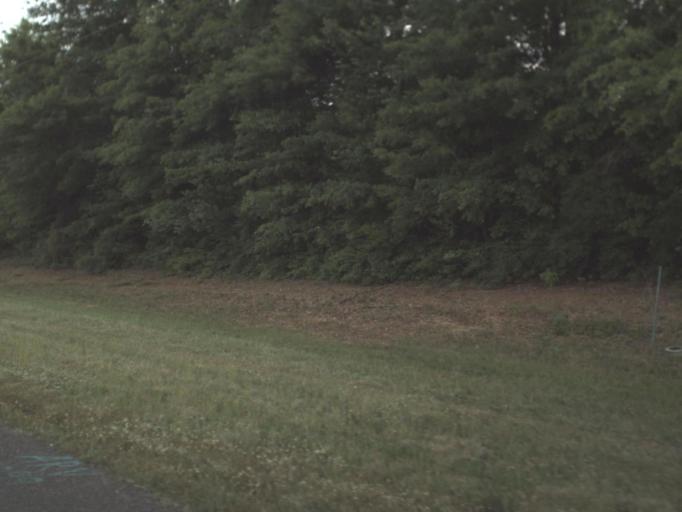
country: US
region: Florida
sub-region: Escambia County
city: Cantonment
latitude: 30.6311
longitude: -87.3341
